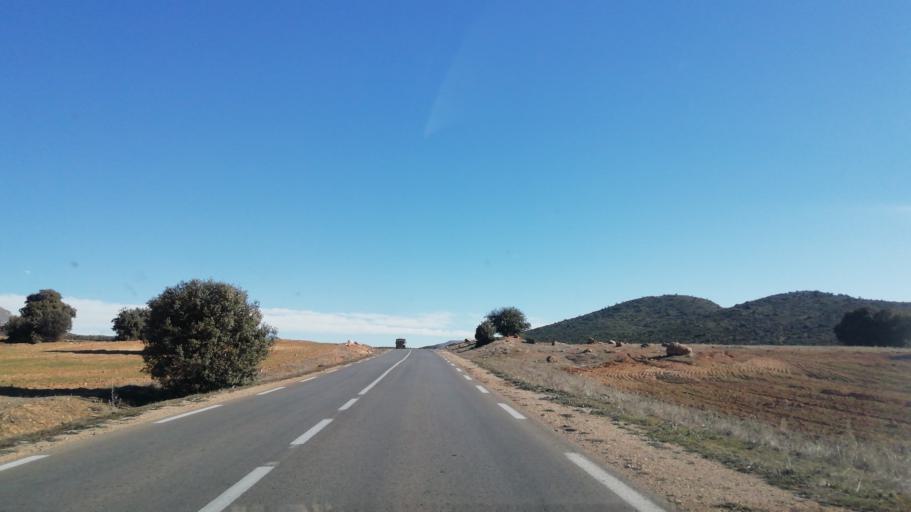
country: DZ
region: Tlemcen
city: Sebdou
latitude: 34.7017
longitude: -1.2244
